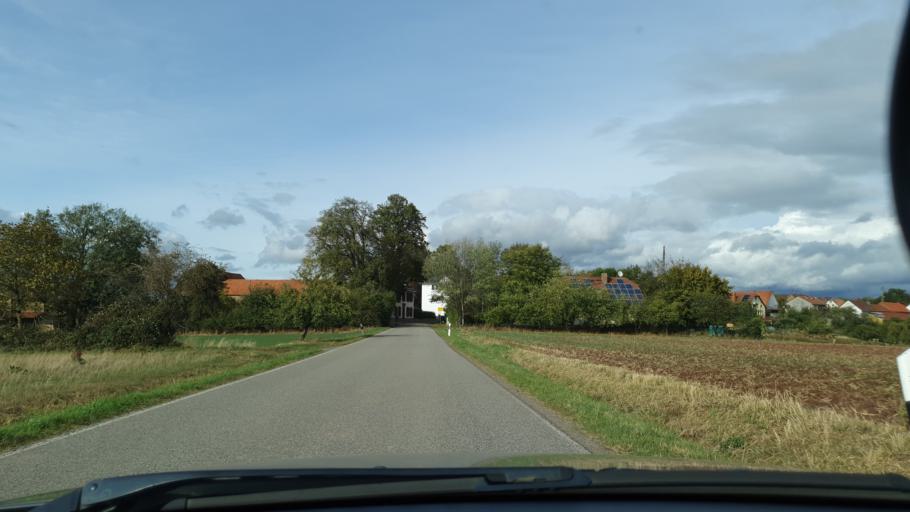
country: DE
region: Rheinland-Pfalz
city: Gerhardsbrunn
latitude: 49.3519
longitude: 7.5171
